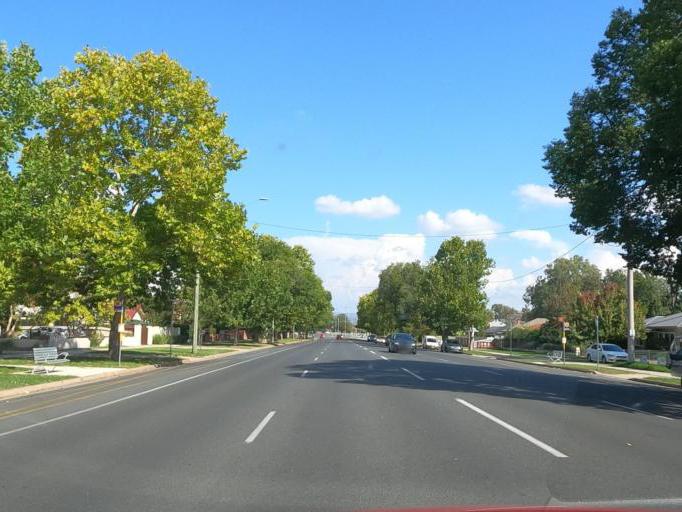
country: AU
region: New South Wales
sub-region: Albury Municipality
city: Albury
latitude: -36.0655
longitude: 146.9244
